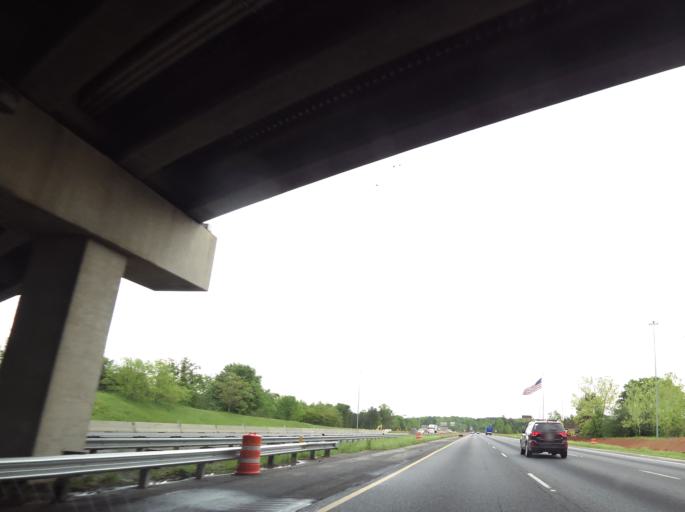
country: US
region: Georgia
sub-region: Henry County
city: McDonough
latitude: 33.4628
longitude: -84.2104
